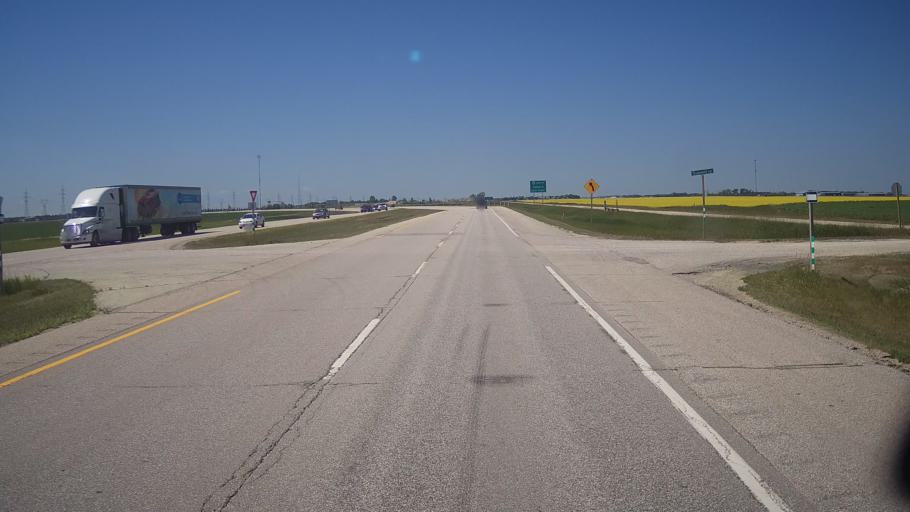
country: CA
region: Manitoba
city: Stonewall
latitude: 49.9900
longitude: -97.2981
